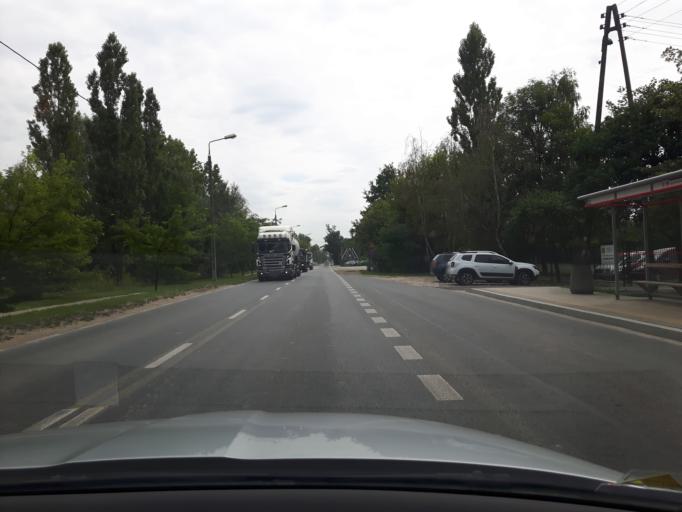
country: PL
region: Masovian Voivodeship
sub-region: Powiat wolominski
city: Zabki
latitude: 52.2735
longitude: 21.1176
